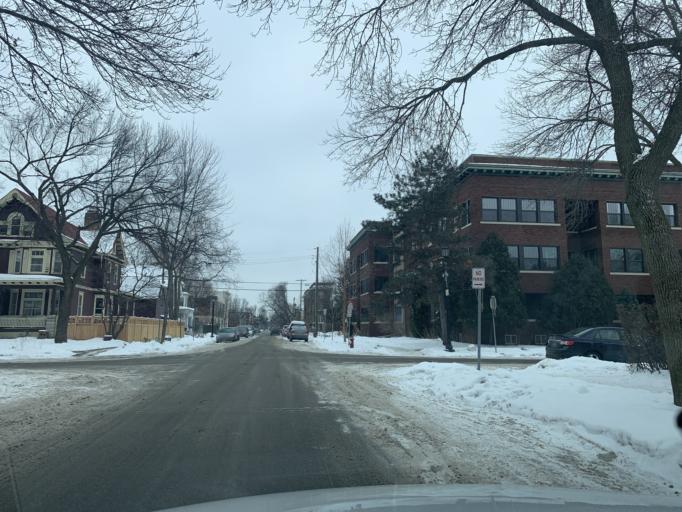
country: US
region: Minnesota
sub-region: Hennepin County
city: Minneapolis
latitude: 44.9591
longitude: -93.2972
